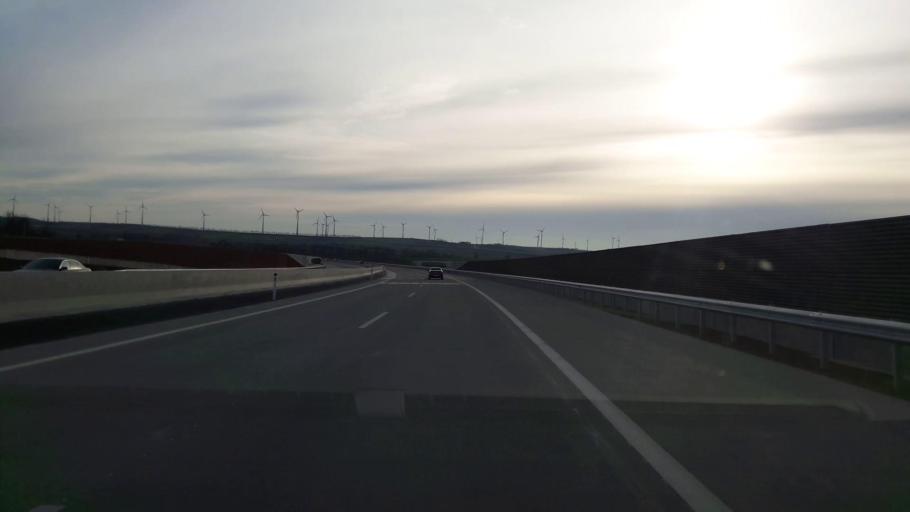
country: AT
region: Lower Austria
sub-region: Politischer Bezirk Mistelbach
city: Wilfersdorf
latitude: 48.5819
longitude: 16.6243
